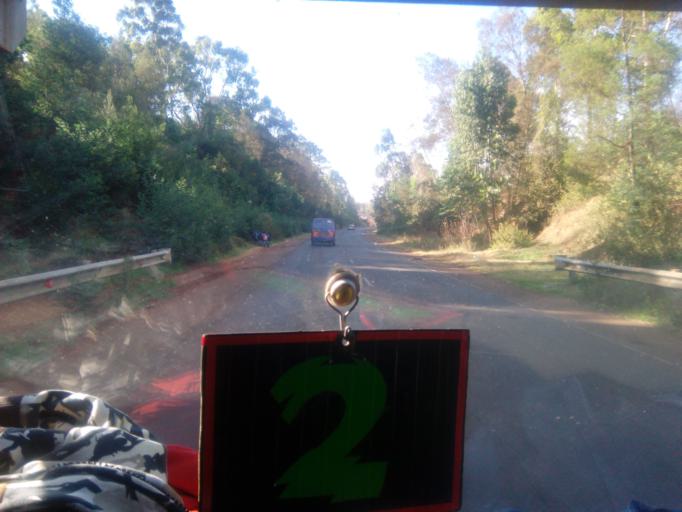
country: KE
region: Kiambu
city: Kikuyu
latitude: -1.2602
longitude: 36.6676
